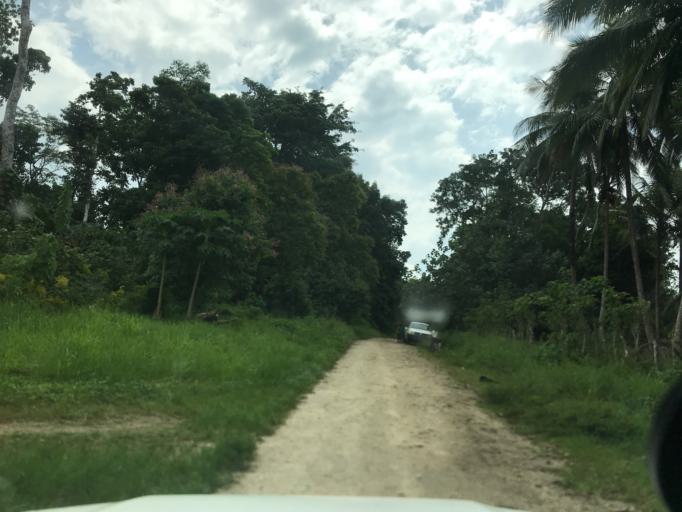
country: VU
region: Sanma
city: Port-Olry
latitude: -15.1730
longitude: 166.9517
